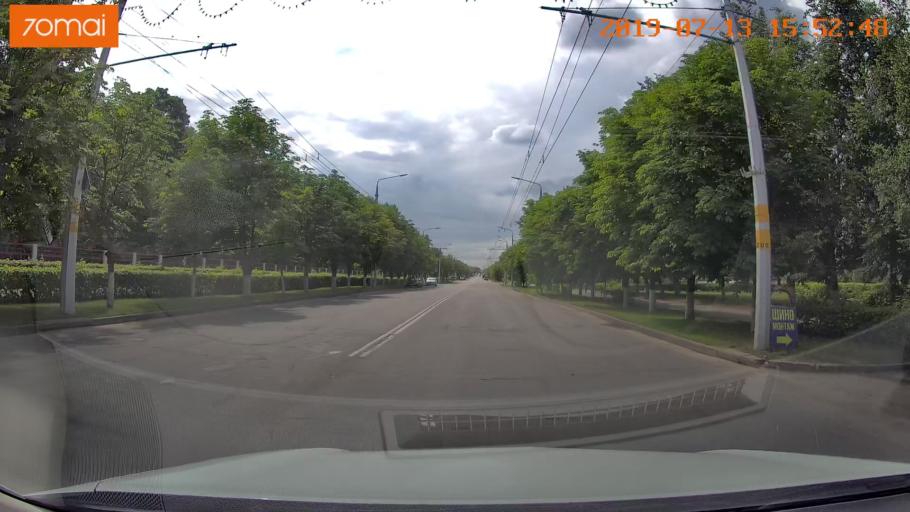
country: BY
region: Mogilev
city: Babruysk
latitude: 53.1390
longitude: 29.2110
